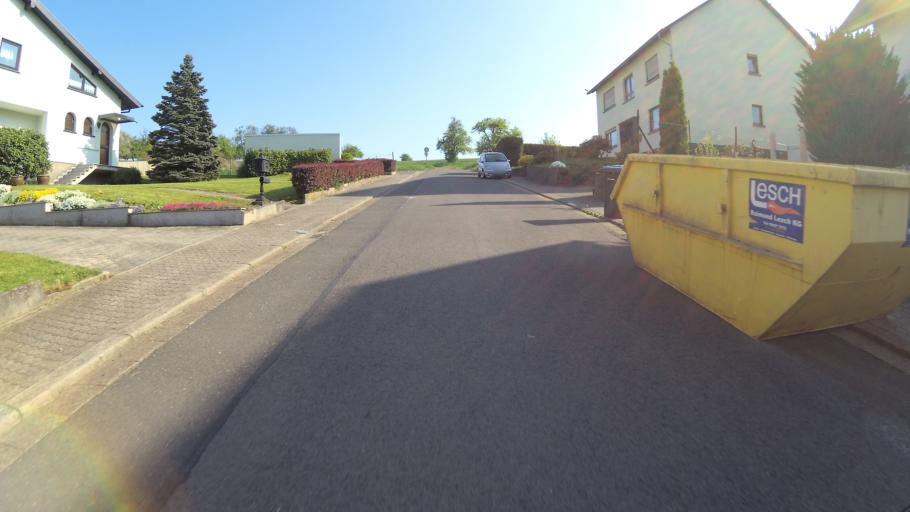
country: DE
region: Saarland
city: Illingen
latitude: 49.3960
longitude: 7.0290
